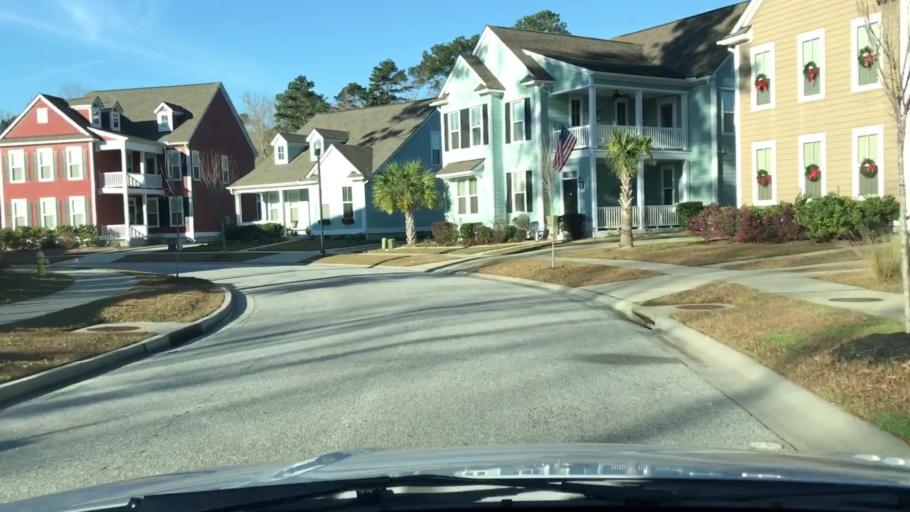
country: US
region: South Carolina
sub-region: Charleston County
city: Shell Point
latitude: 32.8109
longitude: -80.0745
